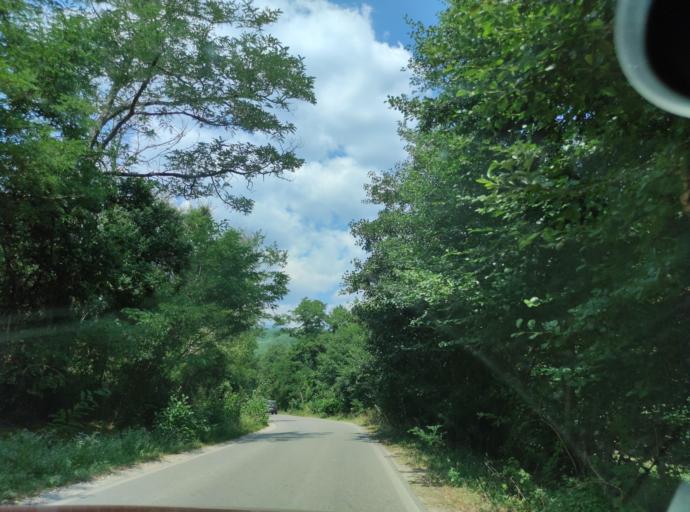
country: BG
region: Blagoevgrad
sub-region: Obshtina Belitsa
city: Belitsa
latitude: 41.9947
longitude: 23.5496
